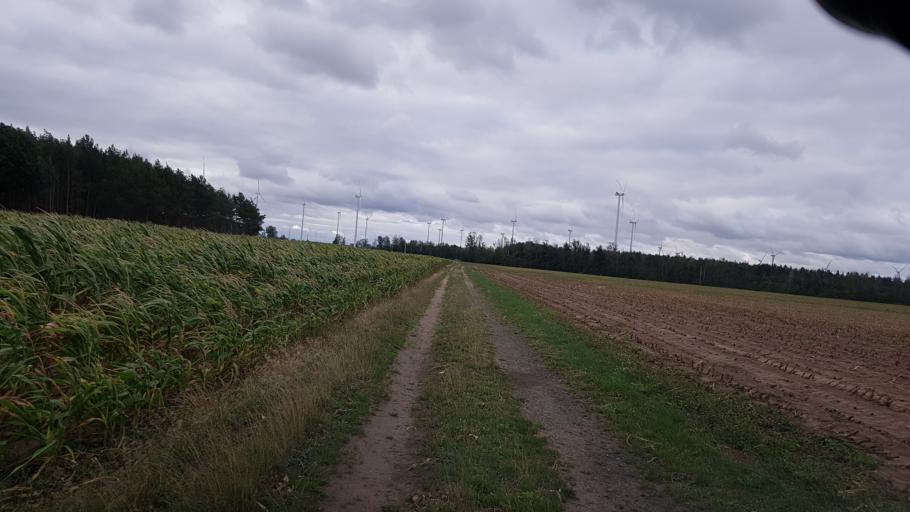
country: DE
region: Brandenburg
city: Bad Liebenwerda
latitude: 51.5453
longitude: 13.3364
